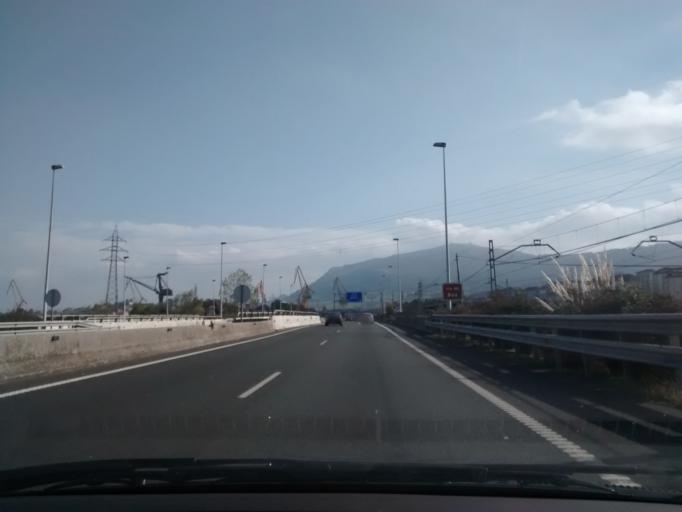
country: ES
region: Cantabria
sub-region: Provincia de Cantabria
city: El Astillero
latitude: 43.4076
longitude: -3.8292
